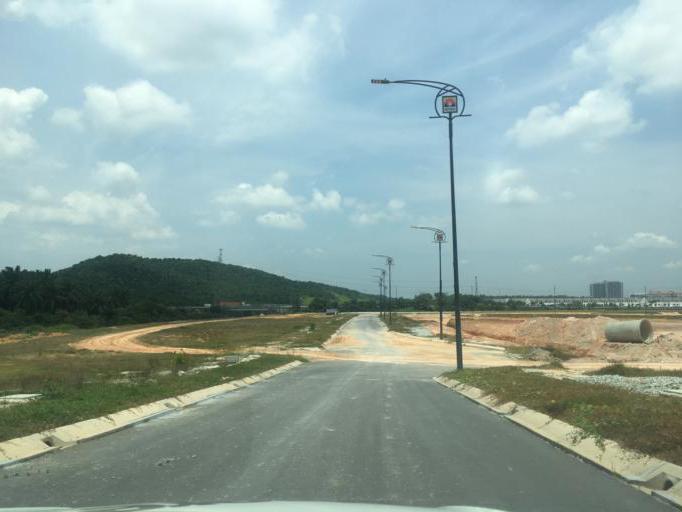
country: MY
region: Putrajaya
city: Putrajaya
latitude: 2.8470
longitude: 101.7107
